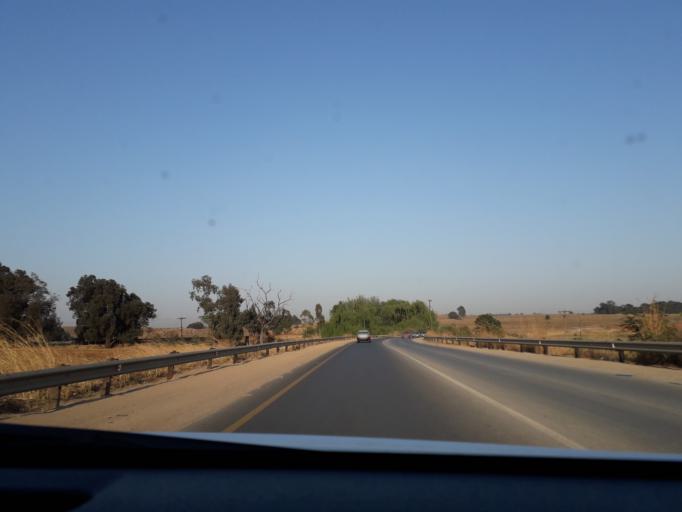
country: ZA
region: Gauteng
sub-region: Ekurhuleni Metropolitan Municipality
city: Tembisa
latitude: -26.0518
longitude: 28.2678
